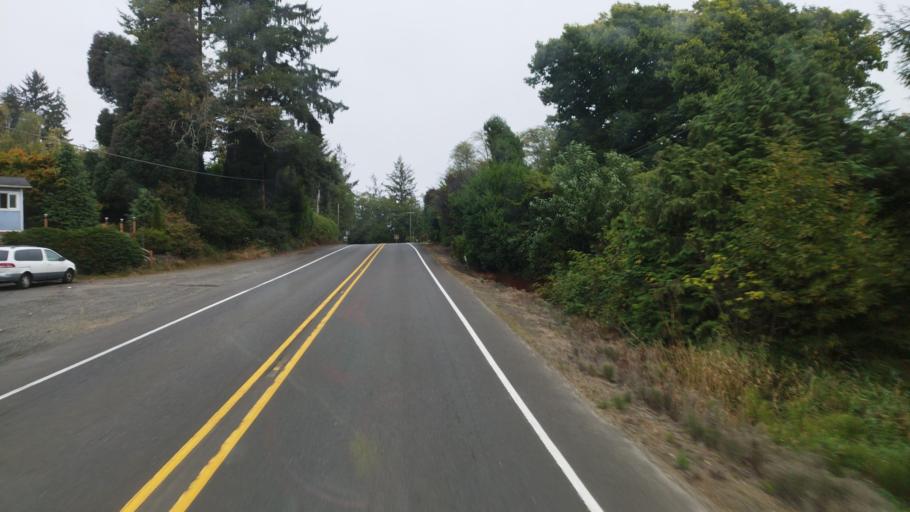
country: US
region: Oregon
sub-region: Clatsop County
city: Astoria
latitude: 46.1771
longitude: -123.7538
